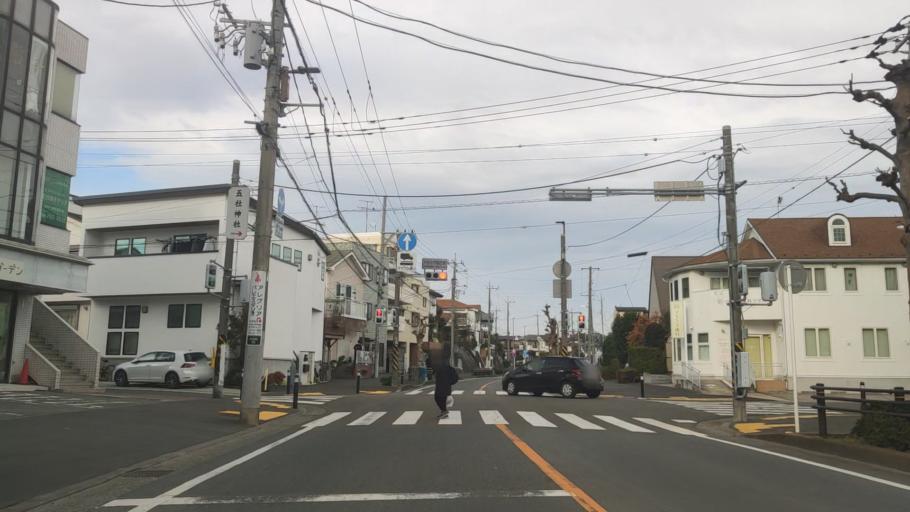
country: JP
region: Kanagawa
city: Atsugi
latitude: 35.4400
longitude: 139.4025
